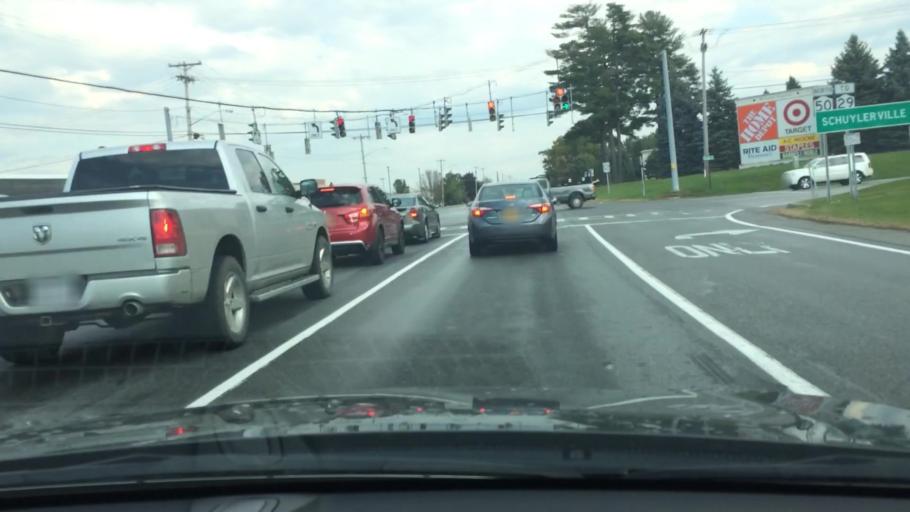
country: US
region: New York
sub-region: Saratoga County
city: Saratoga Springs
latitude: 43.1002
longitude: -73.7476
